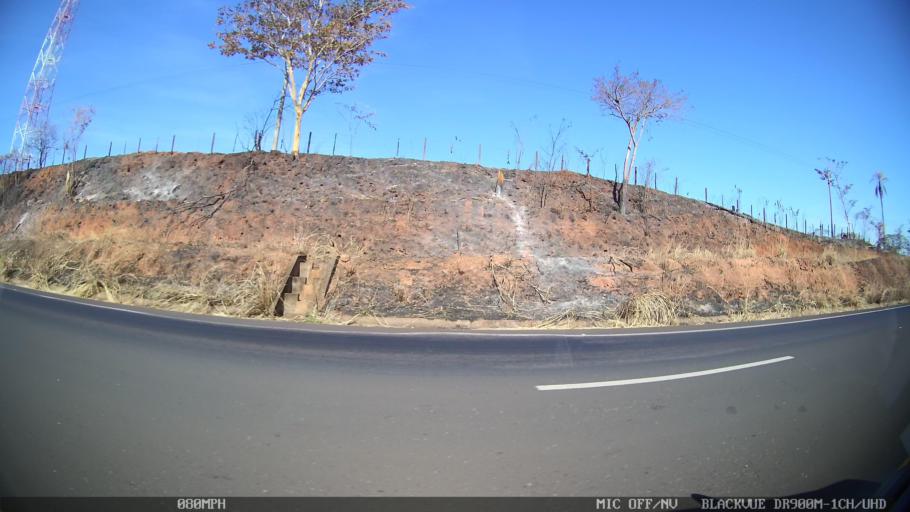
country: BR
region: Sao Paulo
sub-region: Barretos
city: Barretos
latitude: -20.6117
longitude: -48.7537
